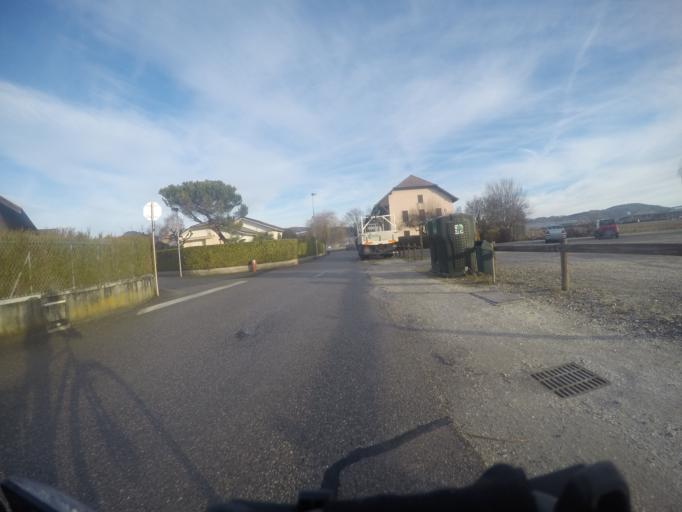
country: FR
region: Rhone-Alpes
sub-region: Departement de la Haute-Savoie
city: Meythet
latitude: 45.9237
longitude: 6.0986
